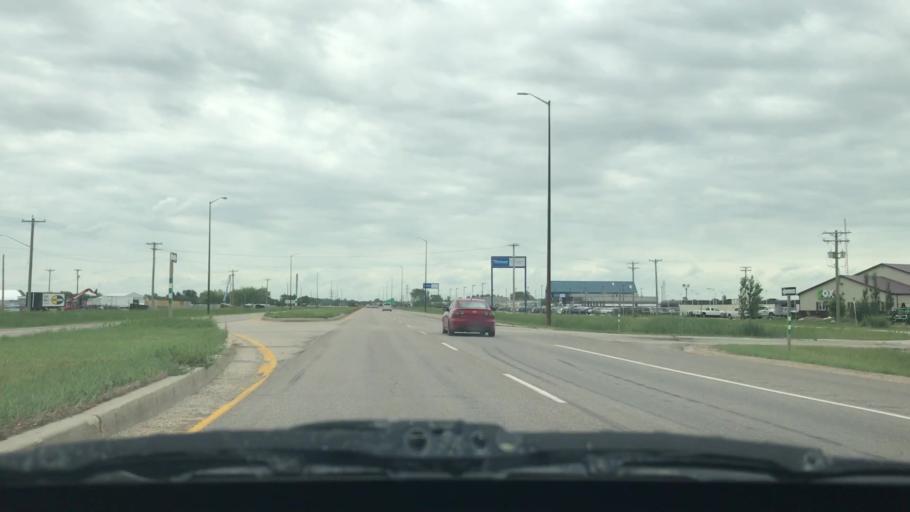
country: CA
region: Manitoba
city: Winnipeg
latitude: 49.8489
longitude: -96.9994
